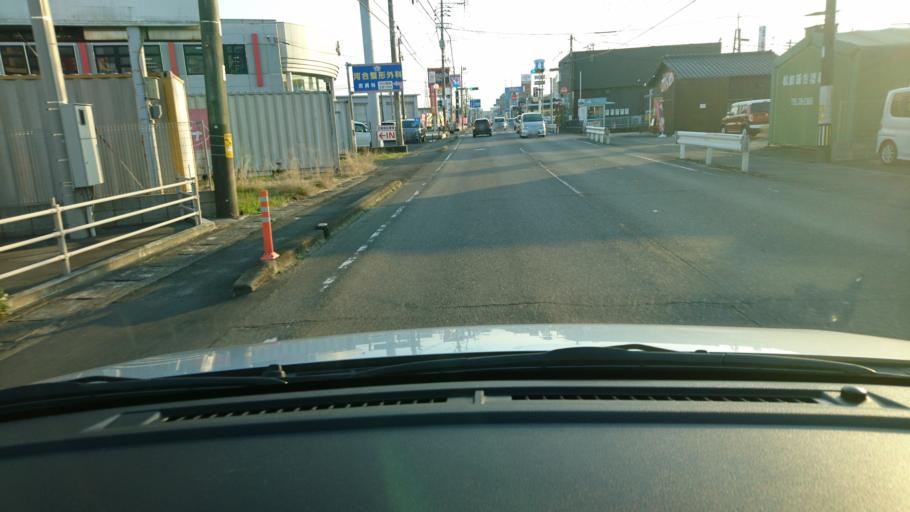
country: JP
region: Miyazaki
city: Miyazaki-shi
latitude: 31.9633
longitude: 131.4388
